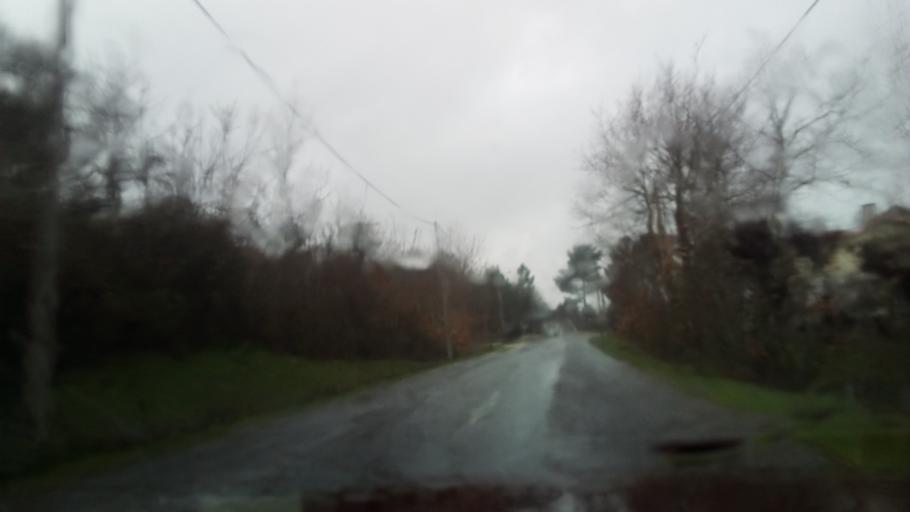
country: PT
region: Guarda
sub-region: Celorico da Beira
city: Celorico da Beira
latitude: 40.6302
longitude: -7.4391
